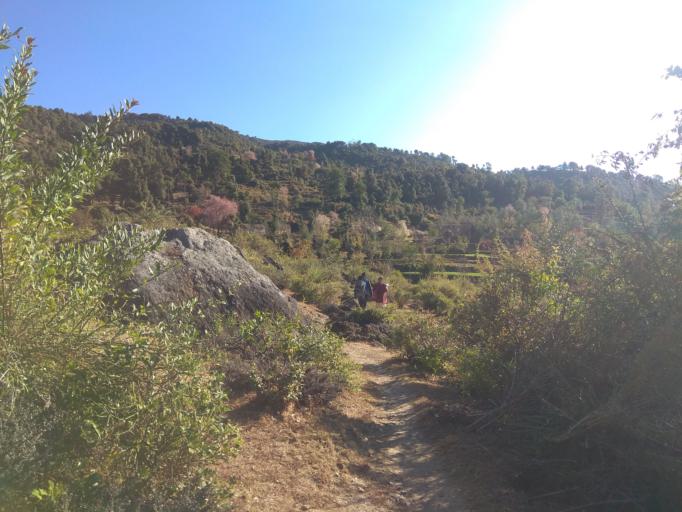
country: NP
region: Far Western
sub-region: Seti Zone
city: Achham
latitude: 29.2766
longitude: 81.6096
